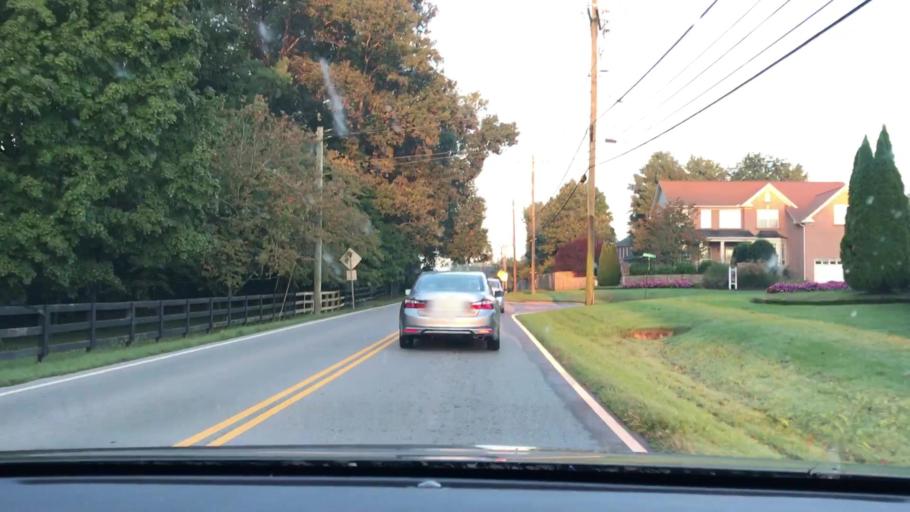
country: US
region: Tennessee
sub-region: Williamson County
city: Brentwood Estates
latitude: 36.0154
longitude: -86.7382
